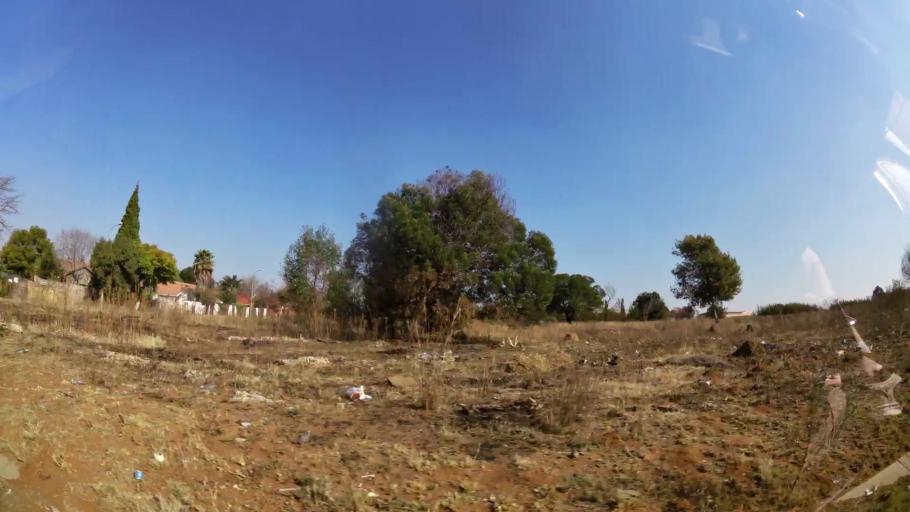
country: ZA
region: Gauteng
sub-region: West Rand District Municipality
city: Randfontein
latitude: -26.1846
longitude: 27.6781
